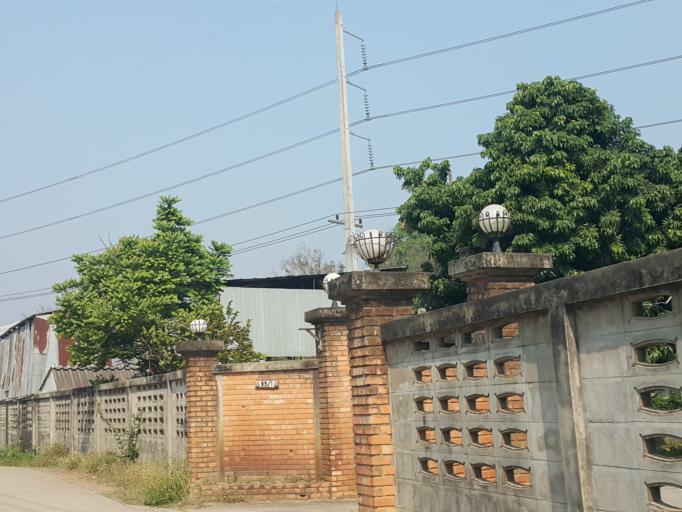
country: TH
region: Chiang Mai
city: Saraphi
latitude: 18.7276
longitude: 99.0213
